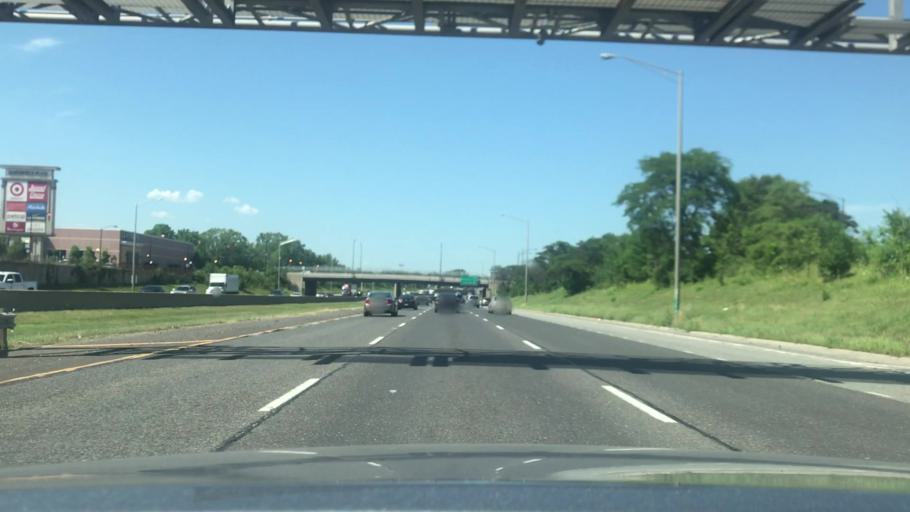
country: US
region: Illinois
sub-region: Cook County
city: Calumet Park
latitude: 41.6824
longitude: -87.6619
